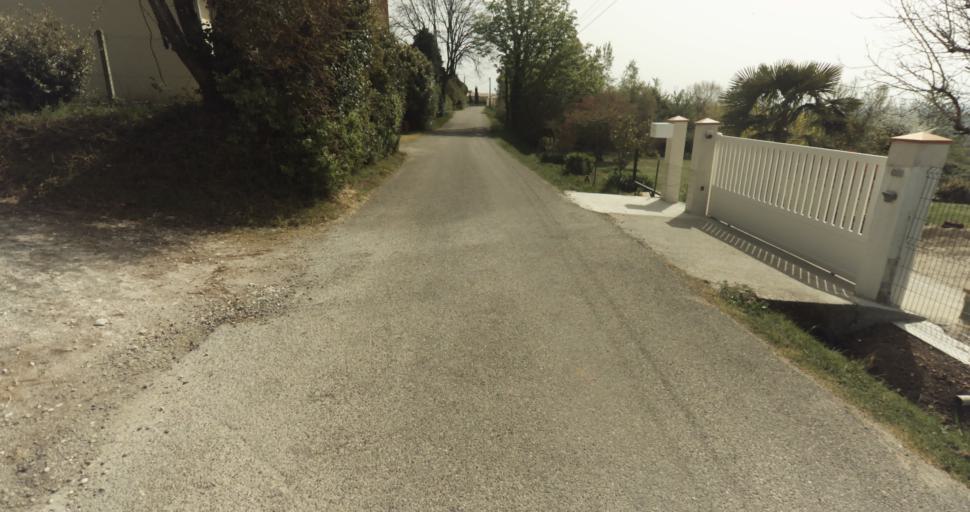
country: FR
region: Midi-Pyrenees
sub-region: Departement du Tarn-et-Garonne
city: Moissac
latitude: 44.1156
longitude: 1.0790
